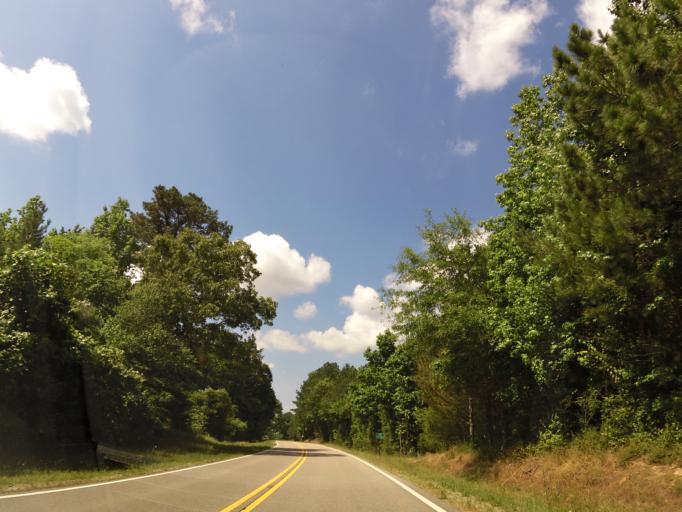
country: US
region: Alabama
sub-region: Marion County
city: Guin
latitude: 33.9889
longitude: -87.8799
